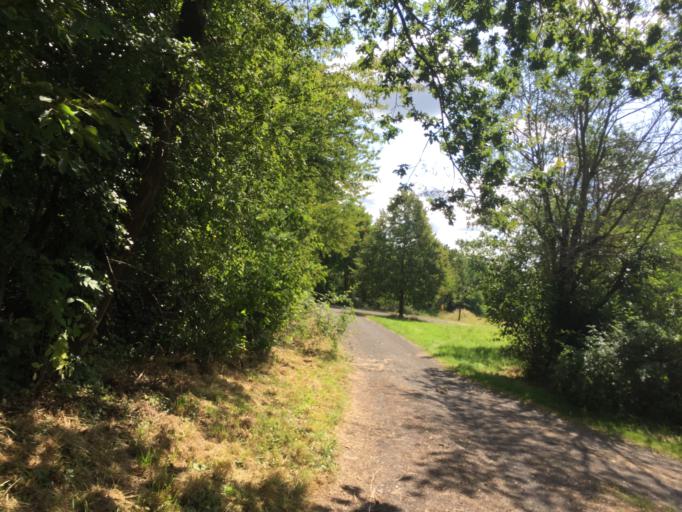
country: DE
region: Hesse
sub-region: Regierungsbezirk Giessen
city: Grunberg
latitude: 50.5819
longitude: 8.9750
